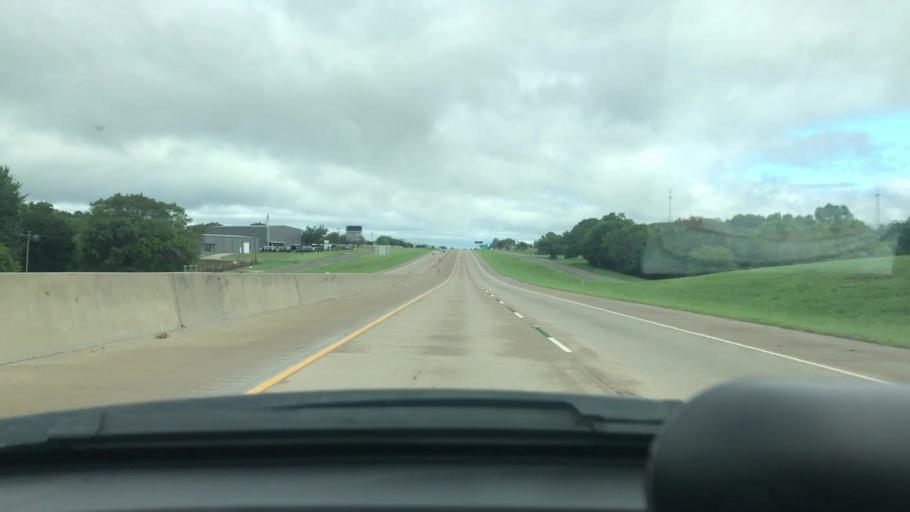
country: US
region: Texas
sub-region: Grayson County
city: Van Alstyne
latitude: 33.4430
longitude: -96.6005
